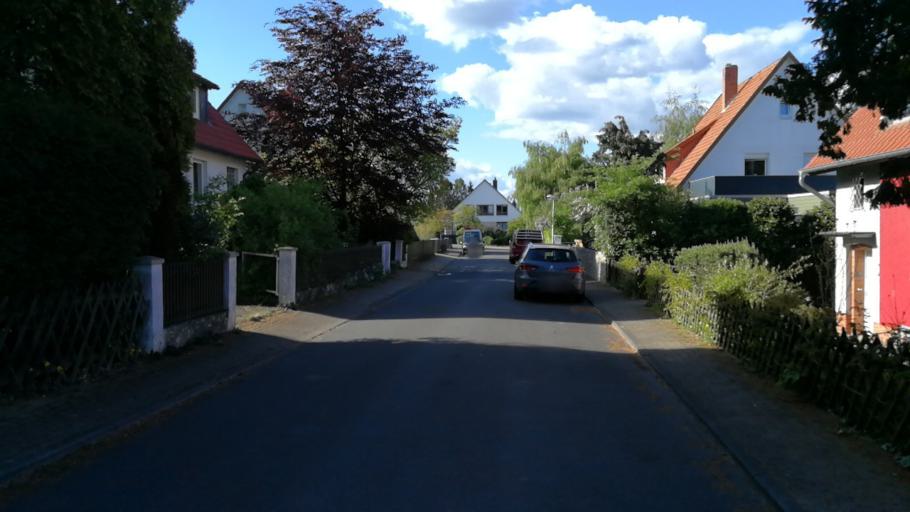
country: DE
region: Lower Saxony
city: Gehrden
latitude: 52.3110
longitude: 9.5943
